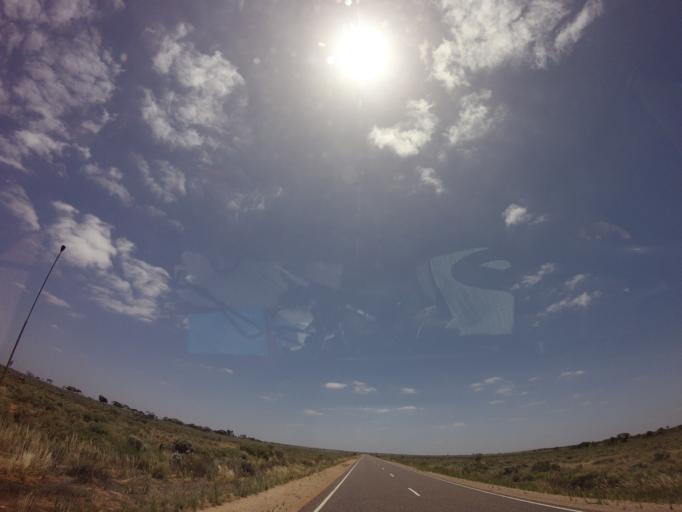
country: AU
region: South Australia
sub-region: Whyalla
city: Whyalla
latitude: -32.8570
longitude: 137.0107
